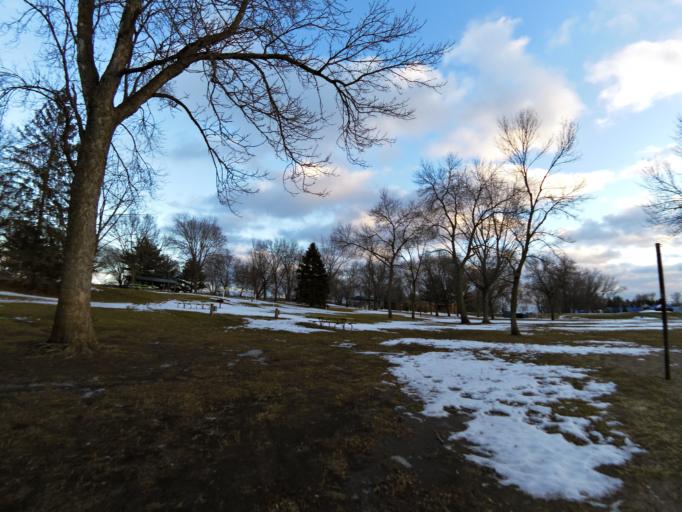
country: US
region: Minnesota
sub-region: Washington County
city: Bayport
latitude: 45.0161
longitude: -92.7740
